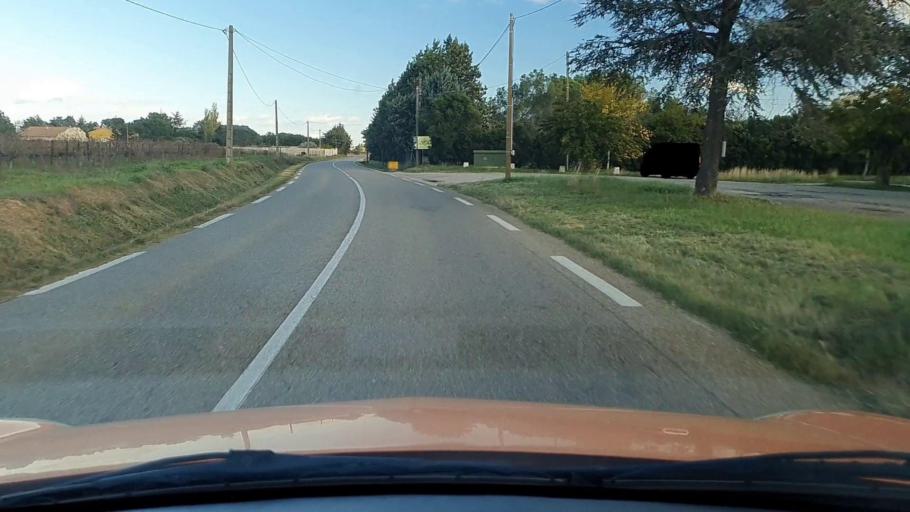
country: FR
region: Languedoc-Roussillon
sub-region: Departement du Gard
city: Saint-Gilles
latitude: 43.6712
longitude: 4.4036
